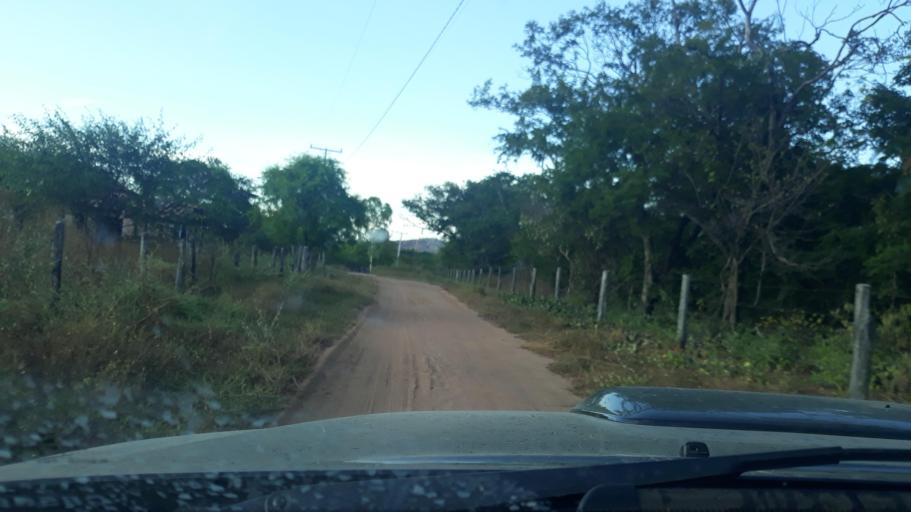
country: BR
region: Bahia
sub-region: Riacho De Santana
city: Riacho de Santana
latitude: -13.8643
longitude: -43.0752
